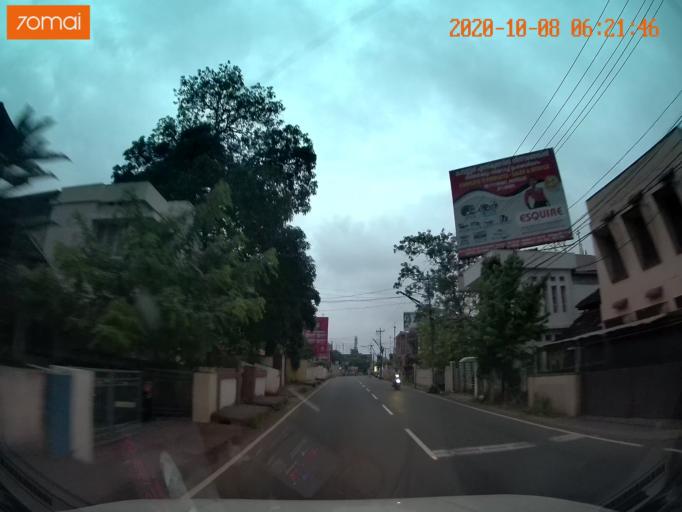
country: IN
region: Kerala
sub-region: Thrissur District
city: Trichur
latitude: 10.5220
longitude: 76.2282
